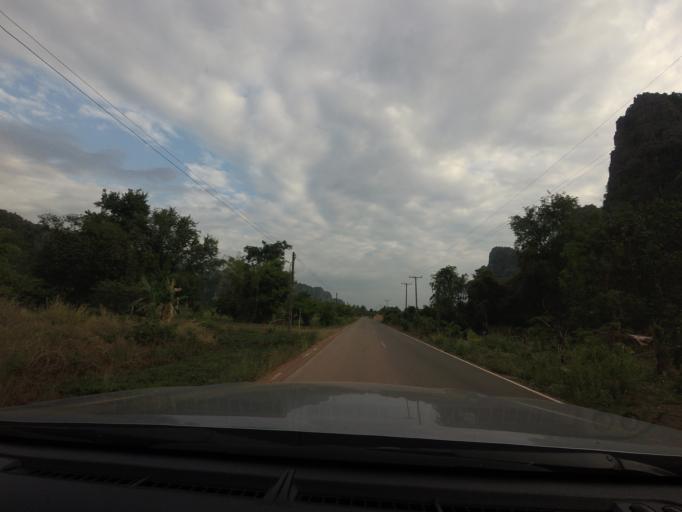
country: TH
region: Phitsanulok
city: Noen Maprang
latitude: 16.5767
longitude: 100.6829
